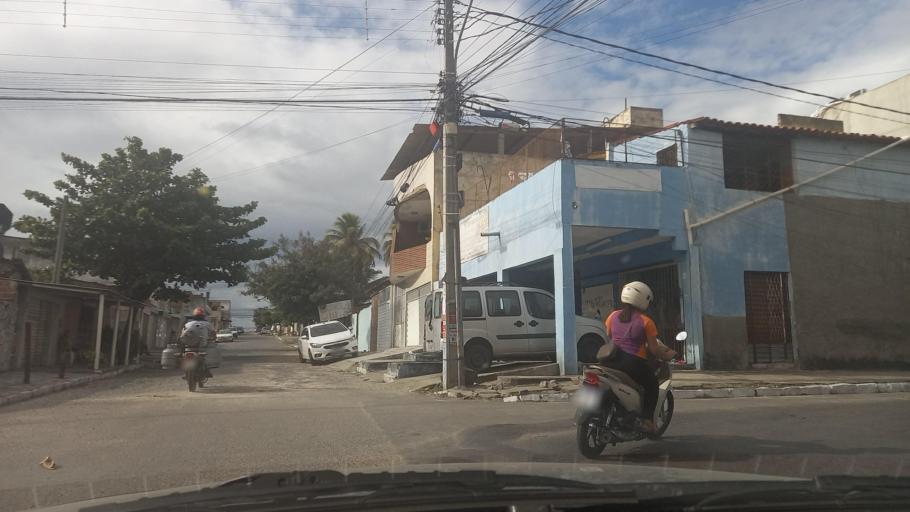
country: BR
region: Pernambuco
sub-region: Caruaru
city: Caruaru
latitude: -8.2848
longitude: -35.9912
